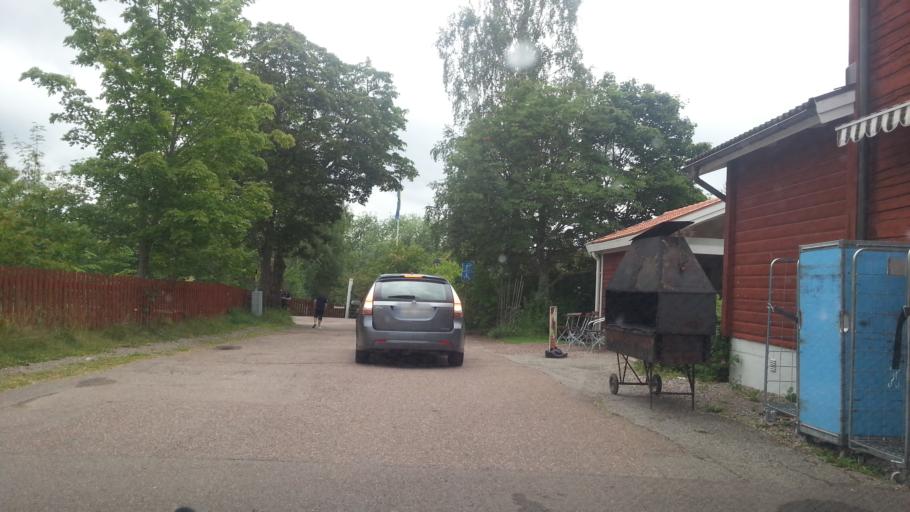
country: SE
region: Dalarna
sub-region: Faluns Kommun
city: Falun
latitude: 60.6509
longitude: 15.7762
